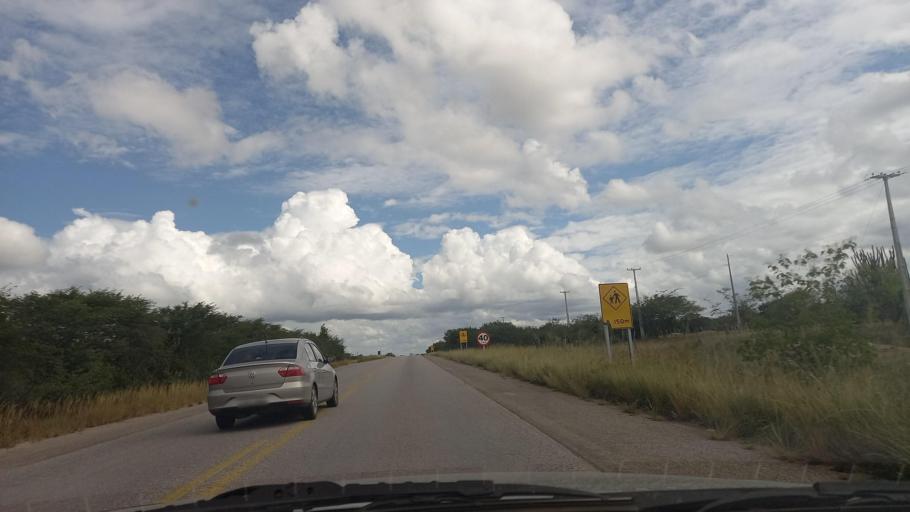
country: BR
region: Pernambuco
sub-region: Cachoeirinha
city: Cachoeirinha
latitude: -8.4276
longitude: -36.1982
